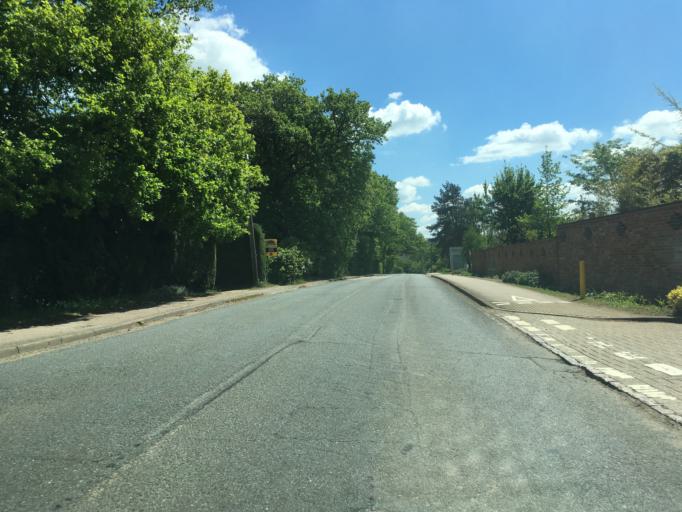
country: GB
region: England
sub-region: Milton Keynes
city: Woburn Sands
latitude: 52.0214
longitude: -0.6585
